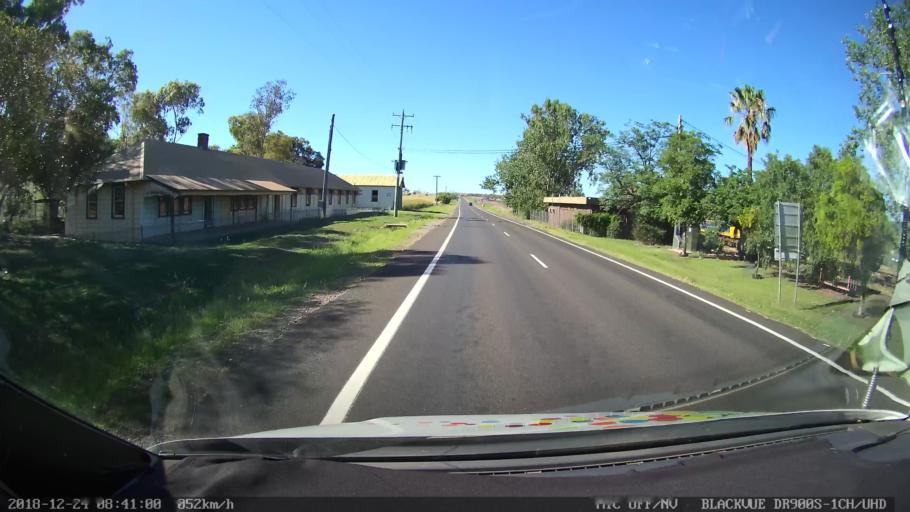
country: AU
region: New South Wales
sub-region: Liverpool Plains
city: Quirindi
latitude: -31.3590
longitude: 150.6456
